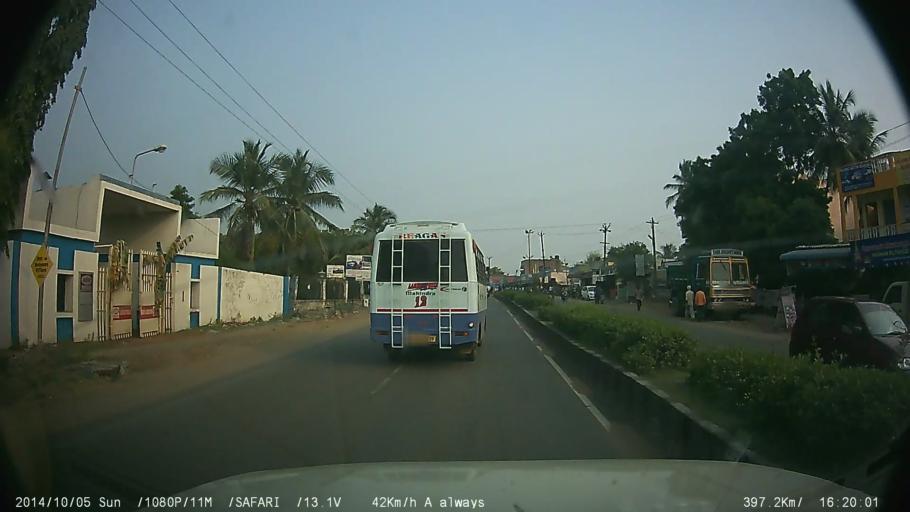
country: IN
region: Tamil Nadu
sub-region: Kancheepuram
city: Vengavasal
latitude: 12.8501
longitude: 80.1415
